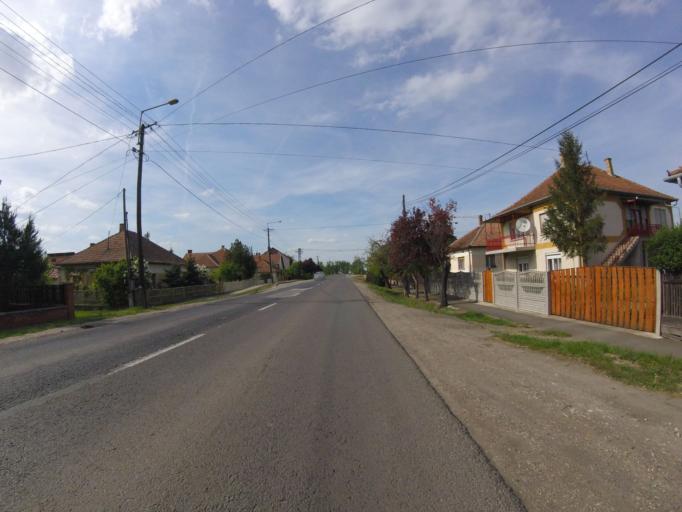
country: HU
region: Jasz-Nagykun-Szolnok
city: Janoshida
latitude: 47.3857
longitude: 20.0731
